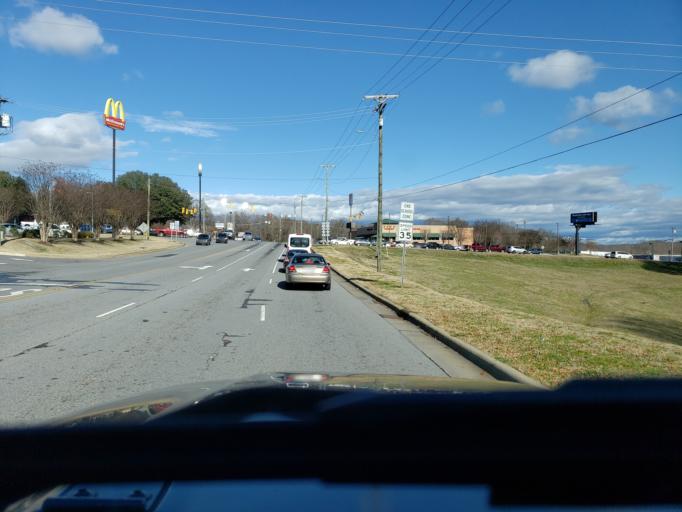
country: US
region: North Carolina
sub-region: Cleveland County
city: Shelby
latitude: 35.2767
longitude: -81.5393
